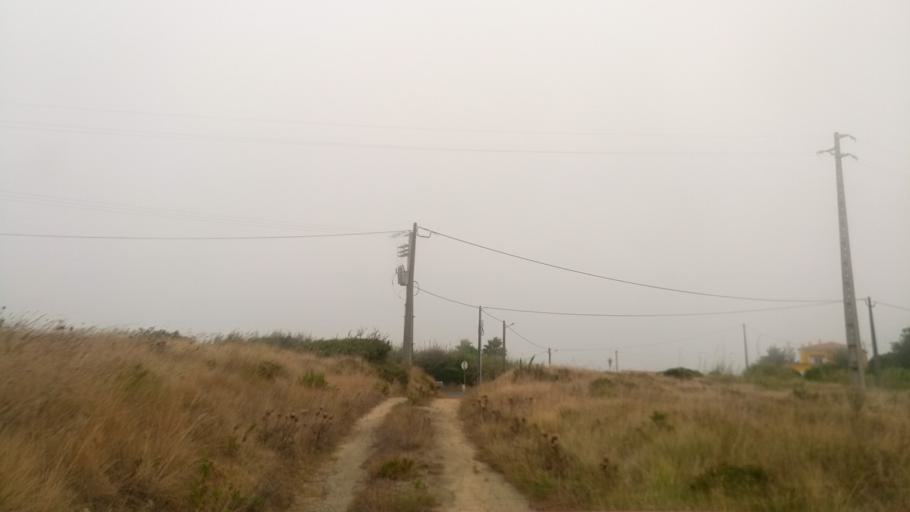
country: PT
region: Leiria
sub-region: Caldas da Rainha
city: Caldas da Rainha
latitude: 39.4652
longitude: -9.1960
